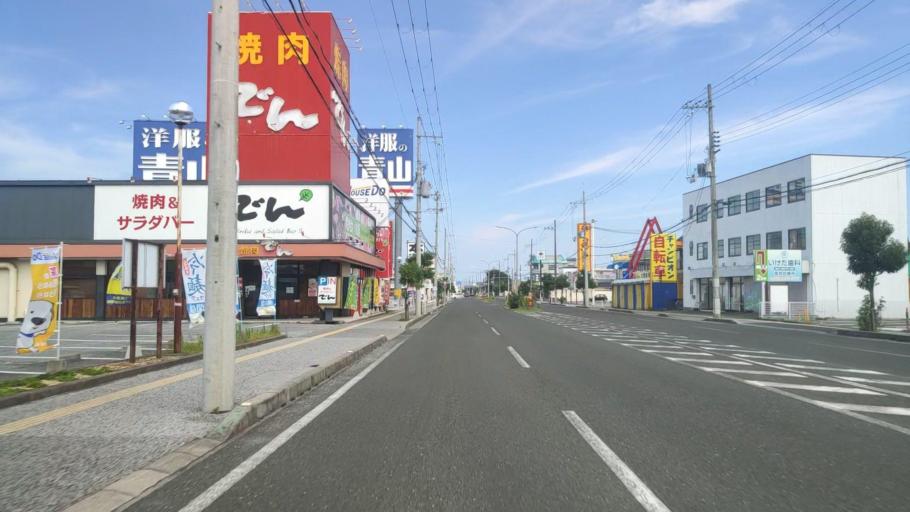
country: JP
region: Shiga Prefecture
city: Hikone
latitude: 35.2521
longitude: 136.2425
